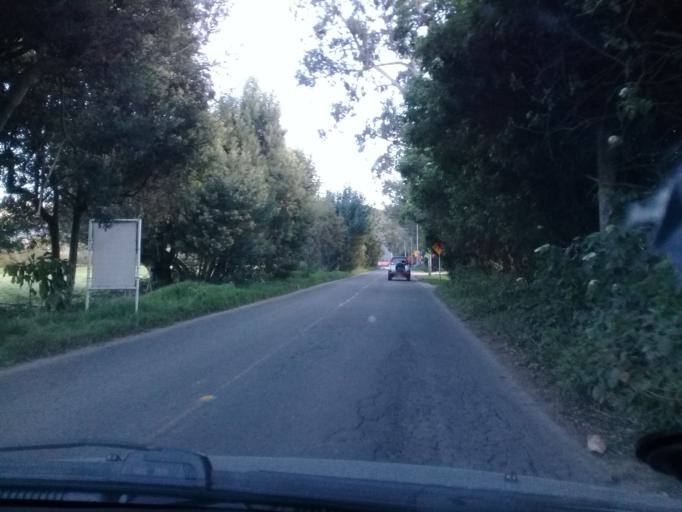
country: CO
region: Cundinamarca
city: Tenjo
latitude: 4.8575
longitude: -74.1353
